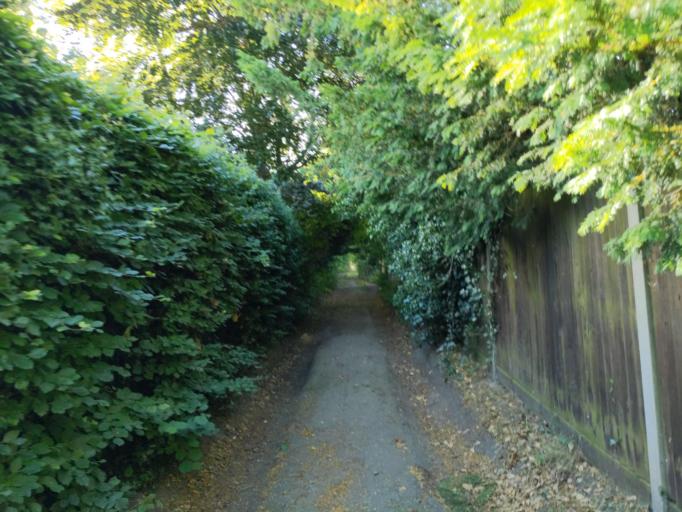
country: GB
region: England
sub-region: Greater London
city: West Wickham
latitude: 51.3756
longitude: 0.0075
